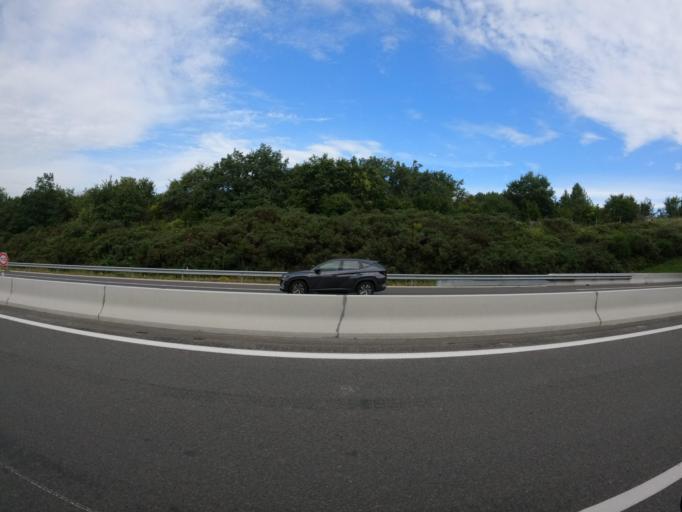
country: FR
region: Centre
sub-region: Departement d'Indre-et-Loire
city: Restigne
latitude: 47.2876
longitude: 0.2829
